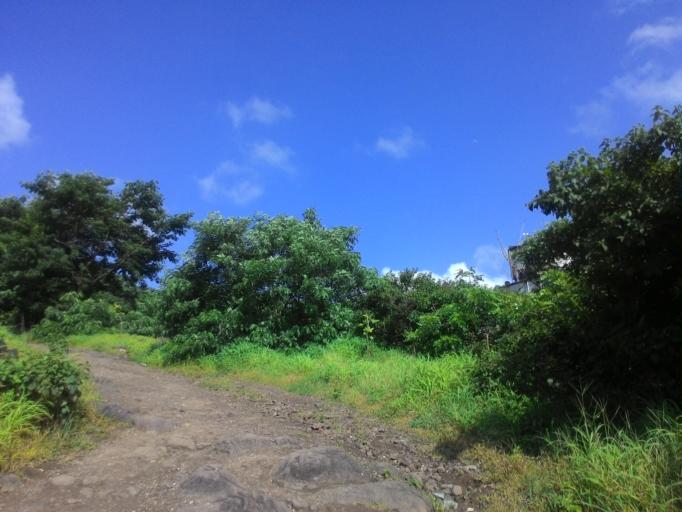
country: IN
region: Maharashtra
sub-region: Pune Division
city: Khadki
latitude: 18.5469
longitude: 73.7746
